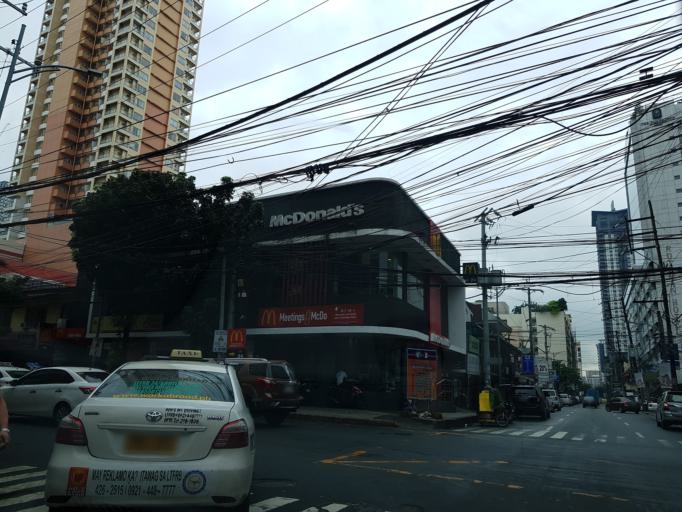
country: PH
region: Metro Manila
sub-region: City of Manila
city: Port Area
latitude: 14.5744
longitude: 120.9838
